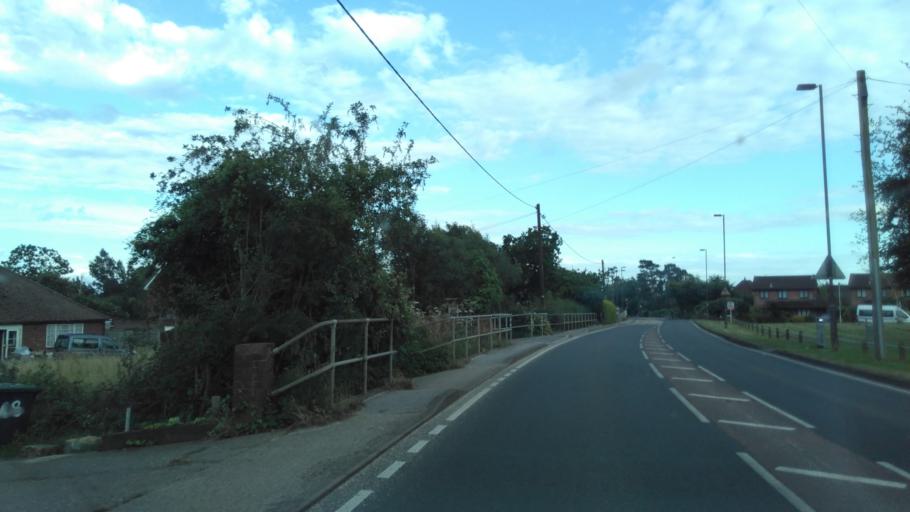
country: GB
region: England
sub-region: Kent
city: Blean
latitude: 51.3081
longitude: 1.0419
